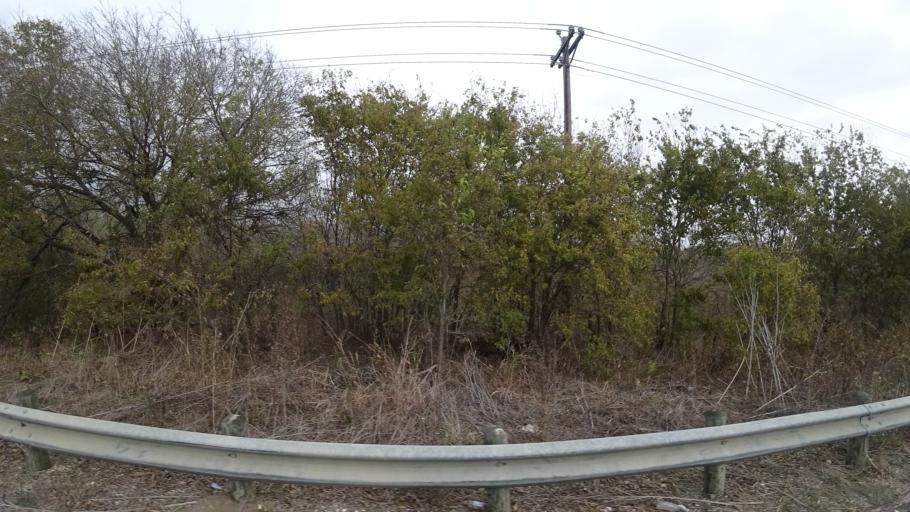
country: US
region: Texas
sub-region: Travis County
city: Manor
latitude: 30.3734
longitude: -97.5731
